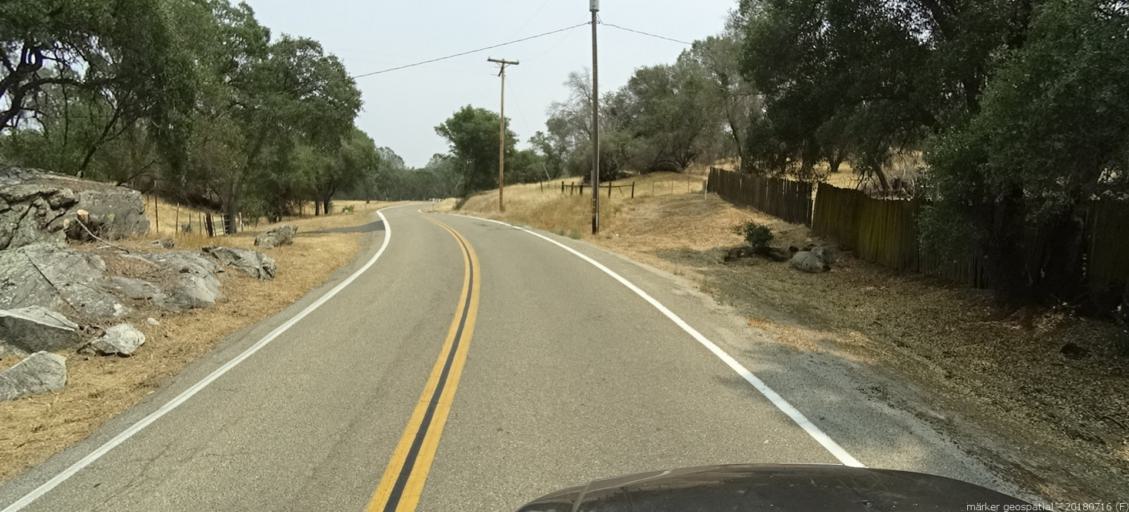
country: US
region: California
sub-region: Madera County
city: Yosemite Lakes
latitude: 37.2418
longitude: -119.8388
